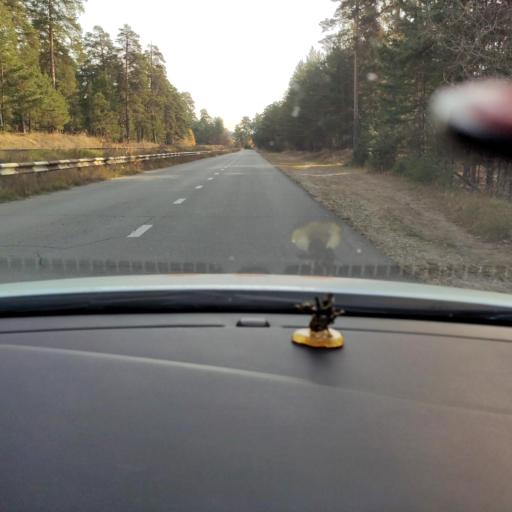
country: RU
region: Tatarstan
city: Osinovo
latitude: 55.8248
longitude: 48.9082
